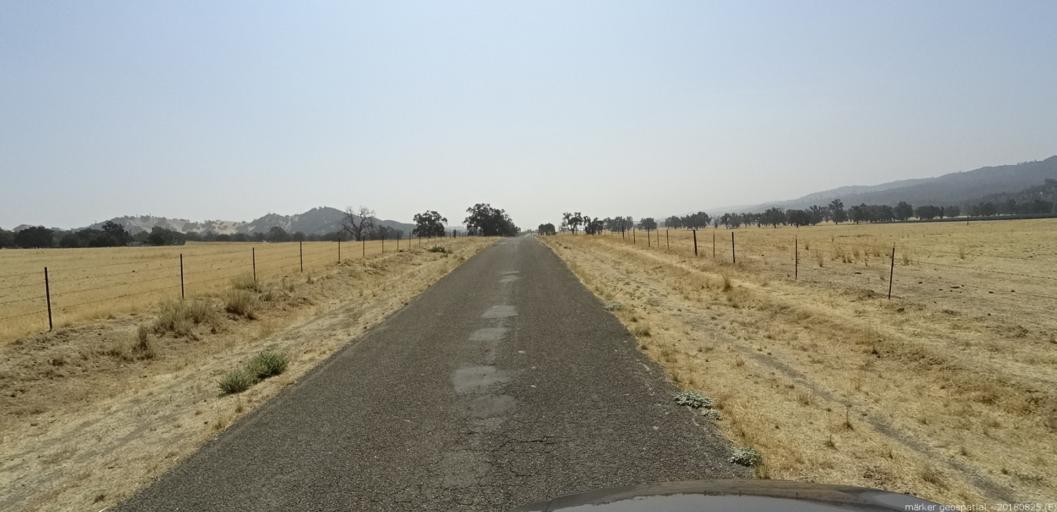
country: US
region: California
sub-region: Fresno County
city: Coalinga
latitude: 35.9532
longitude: -120.5353
